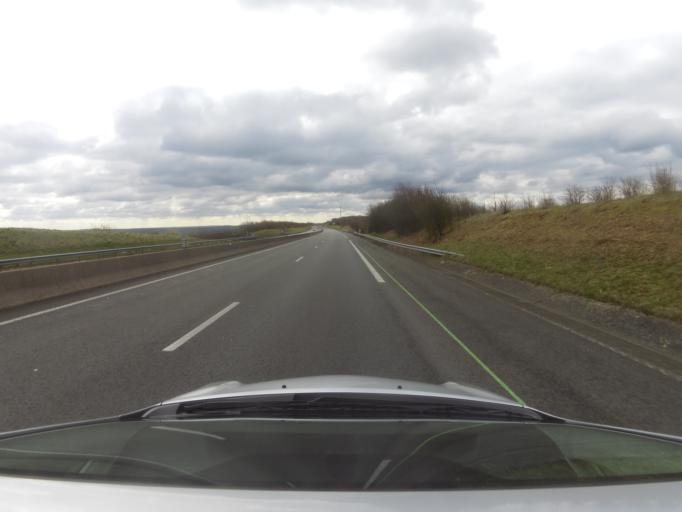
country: FR
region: Nord-Pas-de-Calais
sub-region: Departement du Pas-de-Calais
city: Etaples
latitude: 50.5342
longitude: 1.6810
